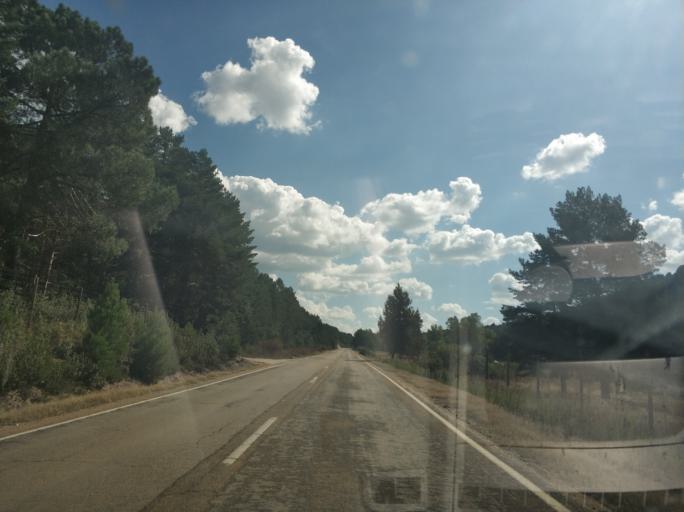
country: ES
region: Castille and Leon
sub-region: Provincia de Soria
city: San Leonardo de Yague
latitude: 41.8124
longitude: -3.0626
